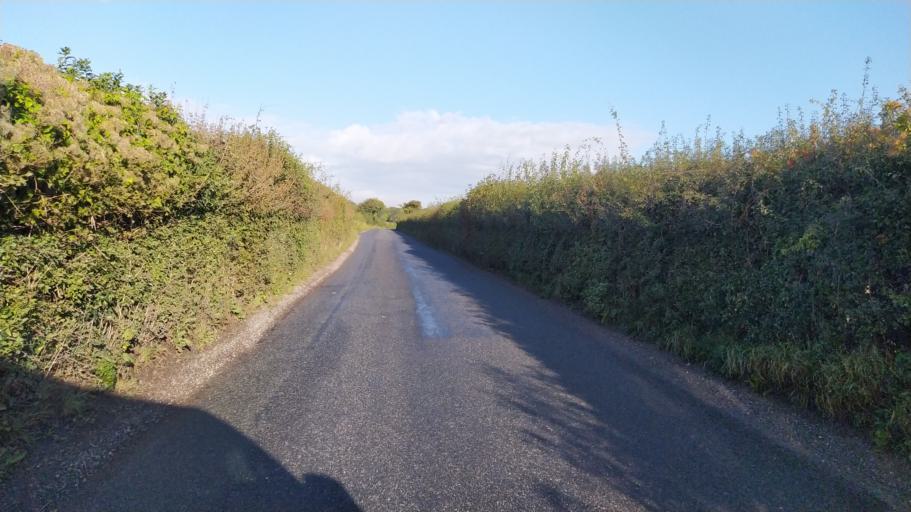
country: GB
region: England
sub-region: Wiltshire
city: Ansty
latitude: 50.9333
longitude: -2.0658
